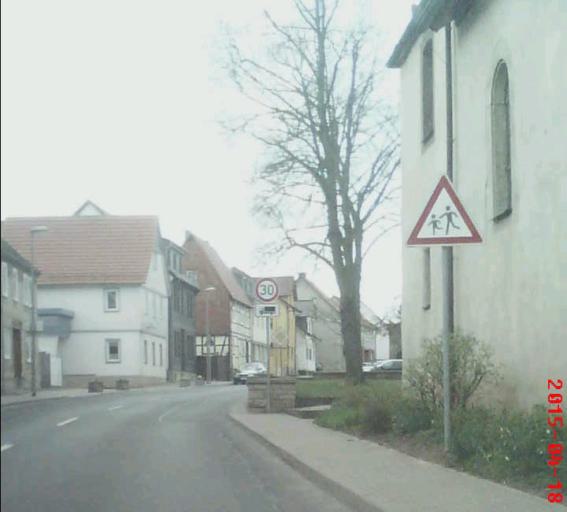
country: DE
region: Thuringia
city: Hausen
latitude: 51.3858
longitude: 10.3558
